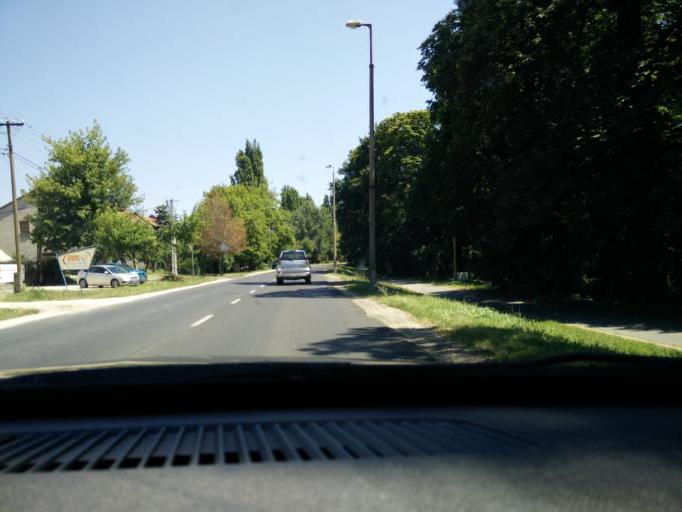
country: HU
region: Komarom-Esztergom
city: Tata
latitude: 47.6450
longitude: 18.3353
